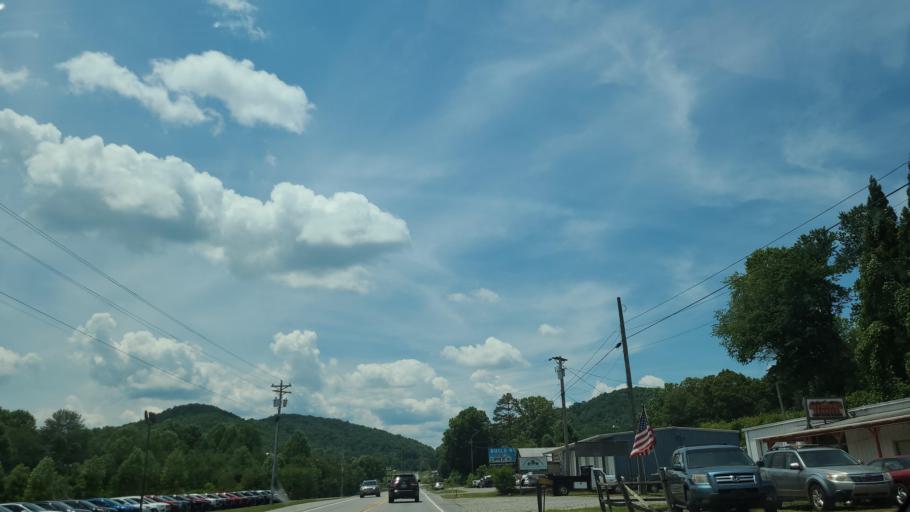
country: US
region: North Carolina
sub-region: Clay County
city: Hayesville
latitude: 35.0339
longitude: -83.8461
